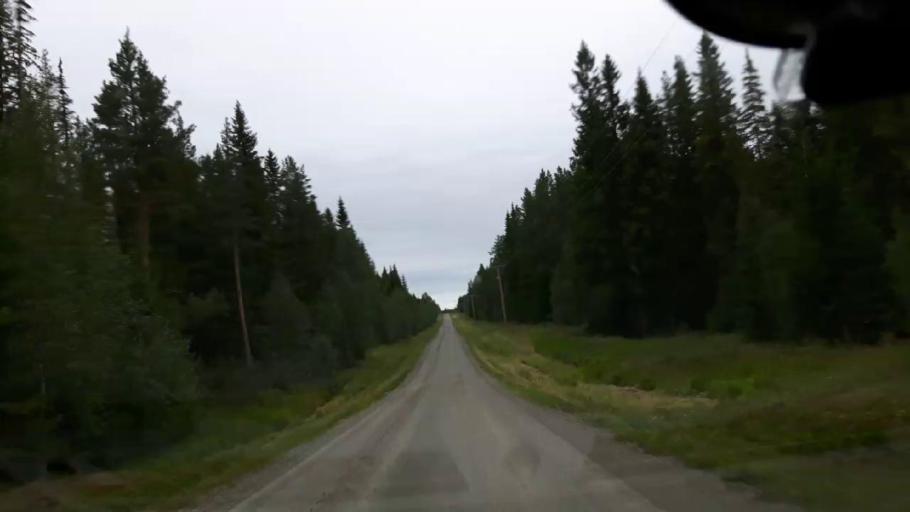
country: SE
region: Vaesternorrland
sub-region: Ange Kommun
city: Fransta
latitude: 62.8010
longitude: 16.0241
